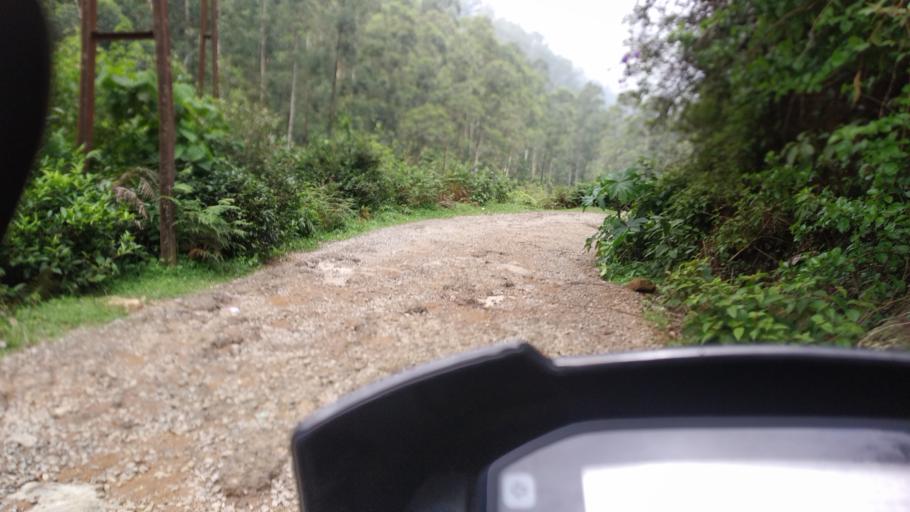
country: IN
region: Kerala
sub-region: Kottayam
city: Erattupetta
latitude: 9.6095
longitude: 76.9708
